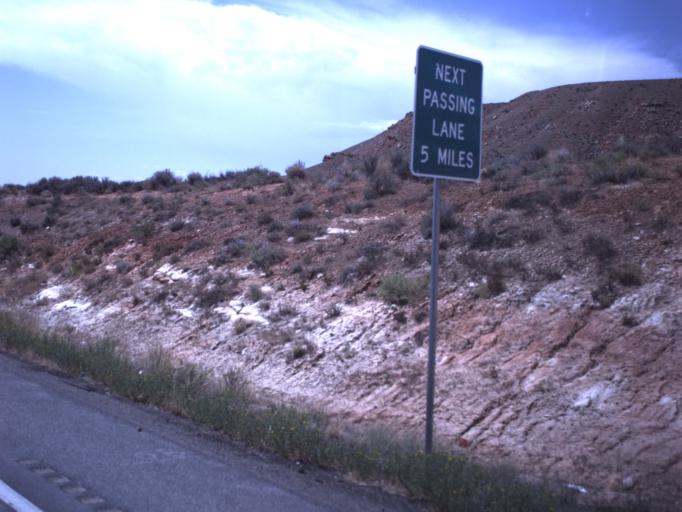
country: US
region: Utah
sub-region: Uintah County
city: Maeser
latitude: 40.3583
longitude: -109.6176
